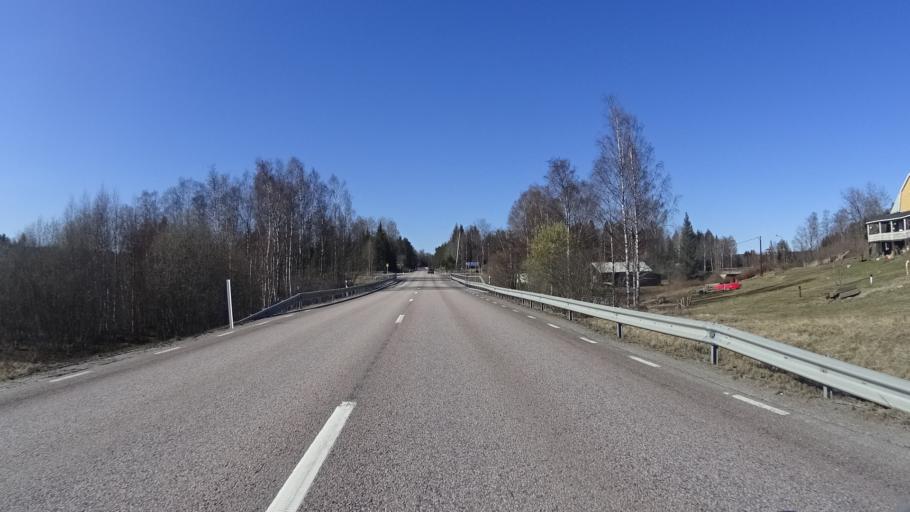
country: SE
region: Vaermland
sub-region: Karlstads Kommun
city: Edsvalla
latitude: 59.5590
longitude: 13.0355
